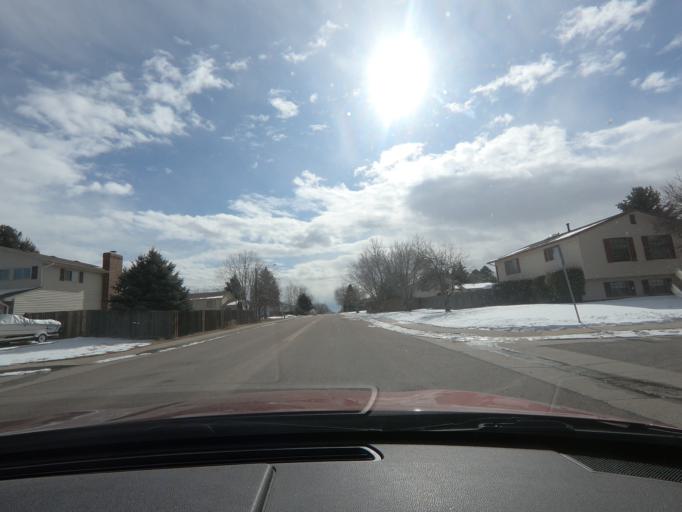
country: US
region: Colorado
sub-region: El Paso County
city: Security-Widefield
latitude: 38.7342
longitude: -104.6884
